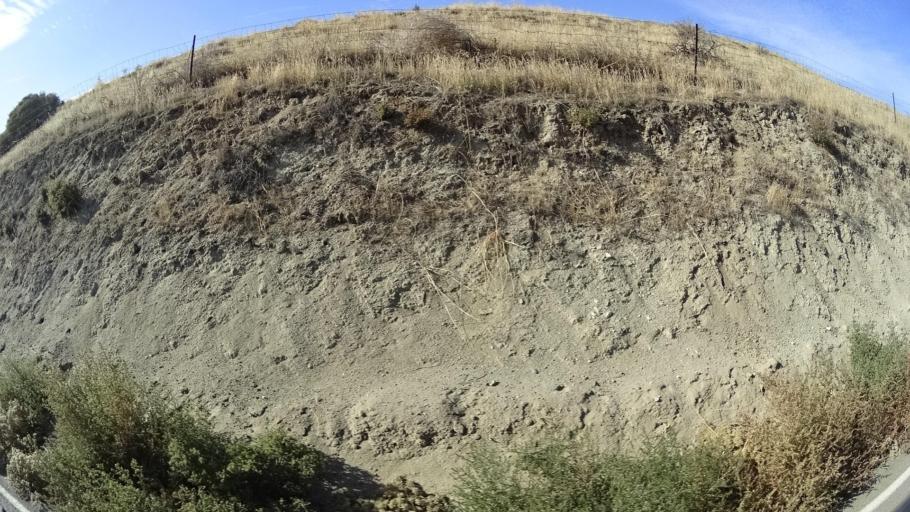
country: US
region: California
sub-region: Kern County
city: Oildale
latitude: 35.5422
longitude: -118.9590
